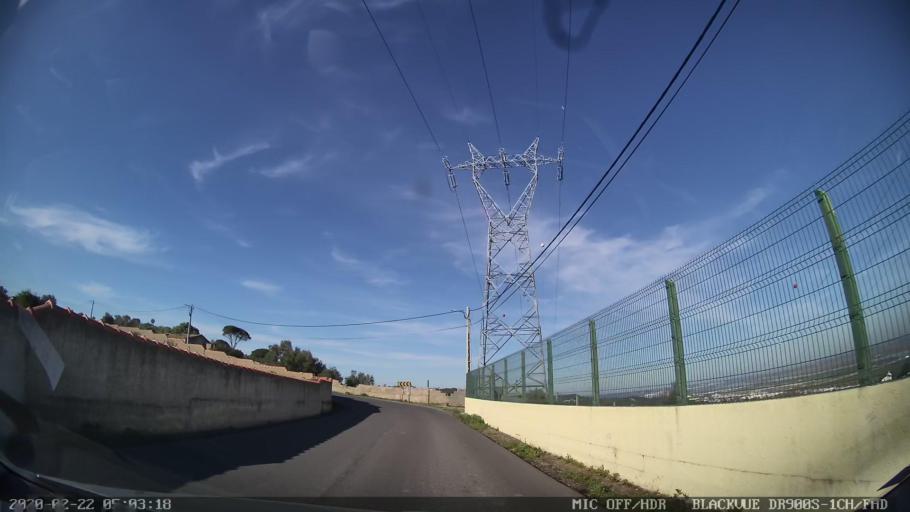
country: PT
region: Lisbon
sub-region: Vila Franca de Xira
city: Vila Franca de Xira
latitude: 38.9694
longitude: -8.9949
